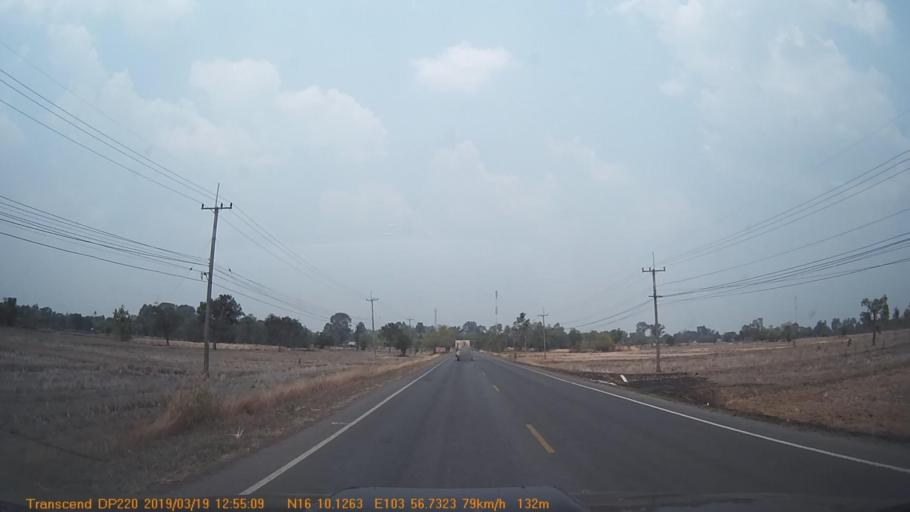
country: TH
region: Roi Et
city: Waeng
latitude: 16.1691
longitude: 103.9455
